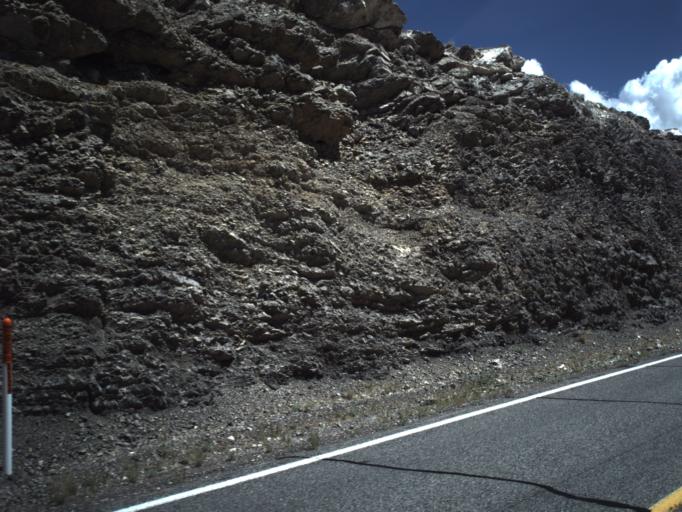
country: US
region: Utah
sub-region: Beaver County
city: Milford
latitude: 39.0788
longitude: -113.6969
